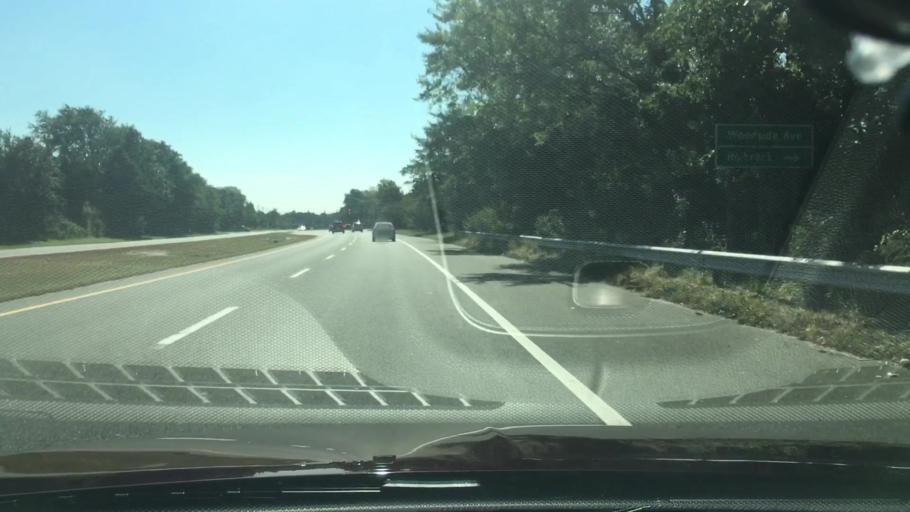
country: US
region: New York
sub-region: Suffolk County
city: North Bellport
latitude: 40.7997
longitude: -72.9596
